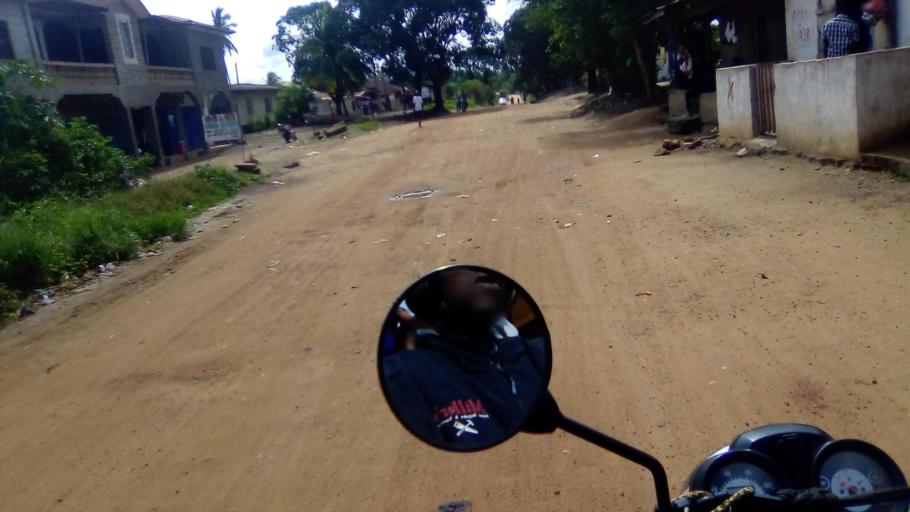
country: SL
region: Southern Province
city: Bo
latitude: 7.9574
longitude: -11.7537
